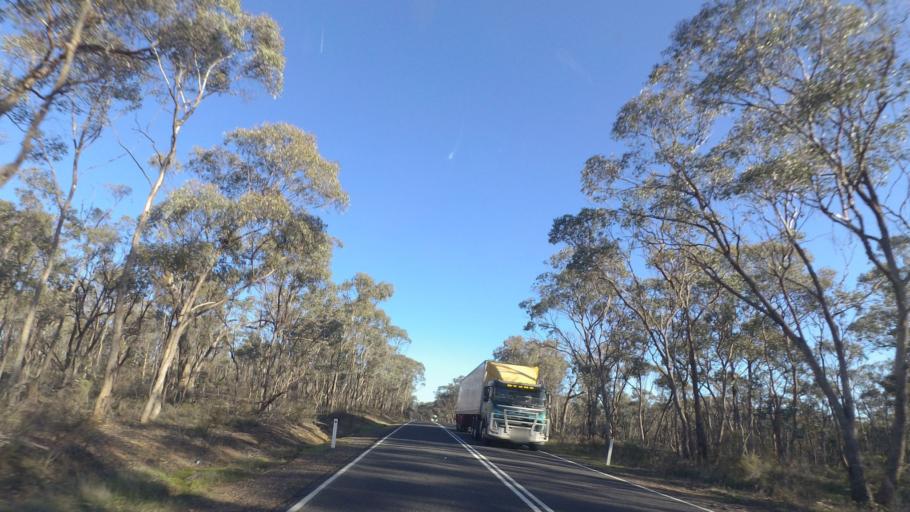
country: AU
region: Victoria
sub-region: Greater Bendigo
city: Kennington
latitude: -36.9061
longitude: 144.4942
